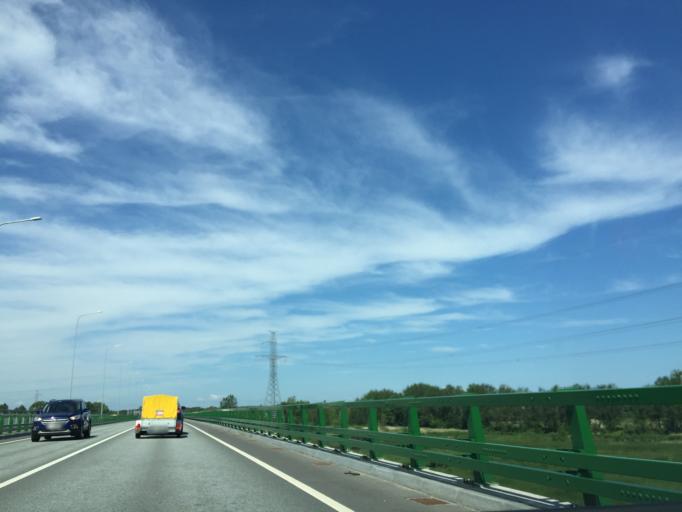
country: LV
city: Tireli
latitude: 56.9304
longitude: 23.6122
